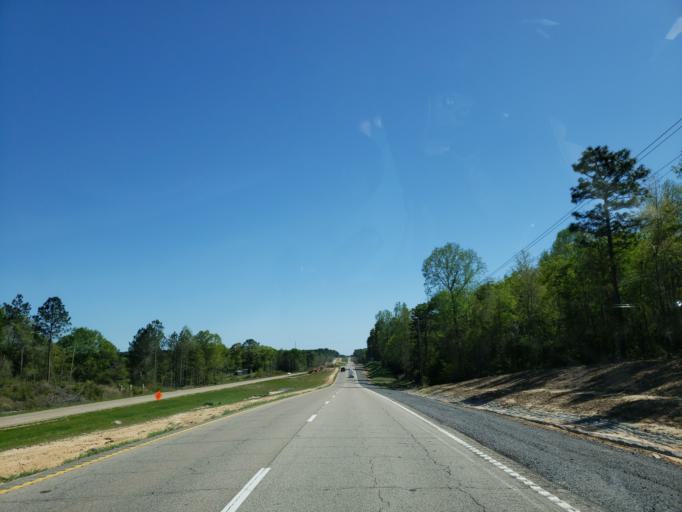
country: US
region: Mississippi
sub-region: Lamar County
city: Purvis
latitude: 31.1648
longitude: -89.2425
